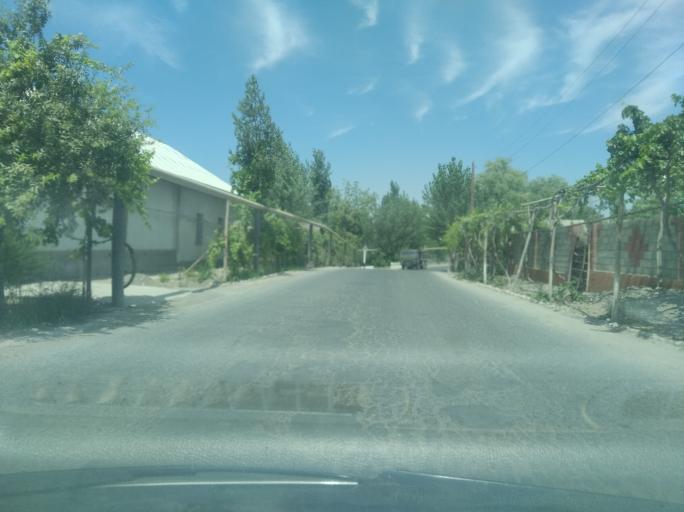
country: UZ
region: Andijon
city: Khujaobod
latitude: 40.6312
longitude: 72.4497
